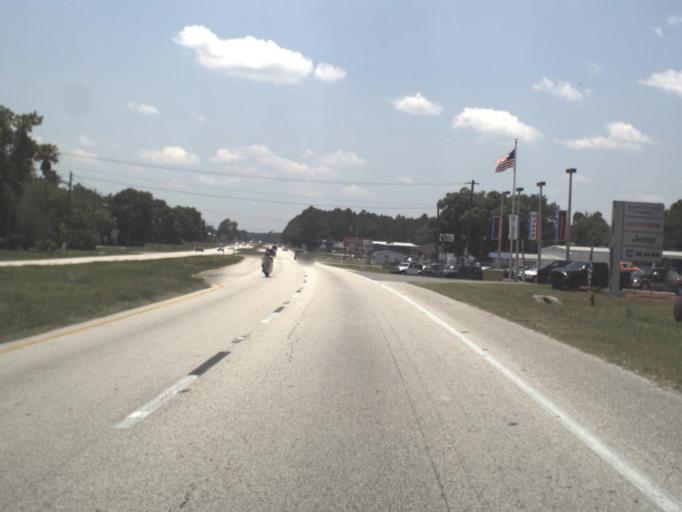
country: US
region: Florida
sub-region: Bradford County
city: Starke
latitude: 29.9286
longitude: -82.1220
